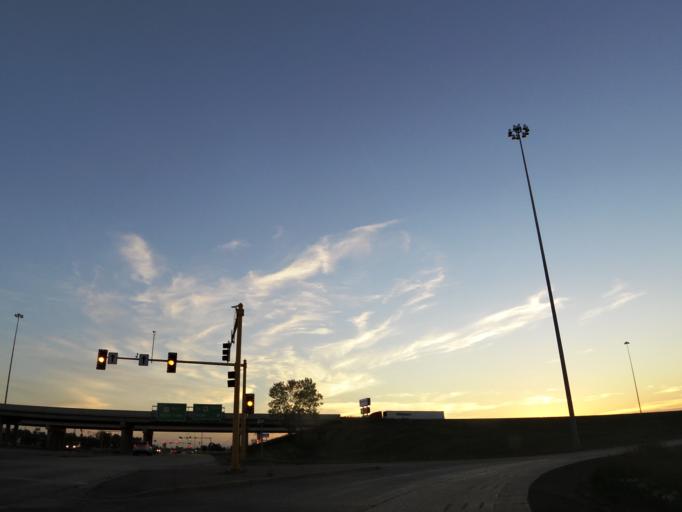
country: US
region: North Dakota
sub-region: Grand Forks County
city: Grand Forks
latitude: 47.9332
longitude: -97.0920
